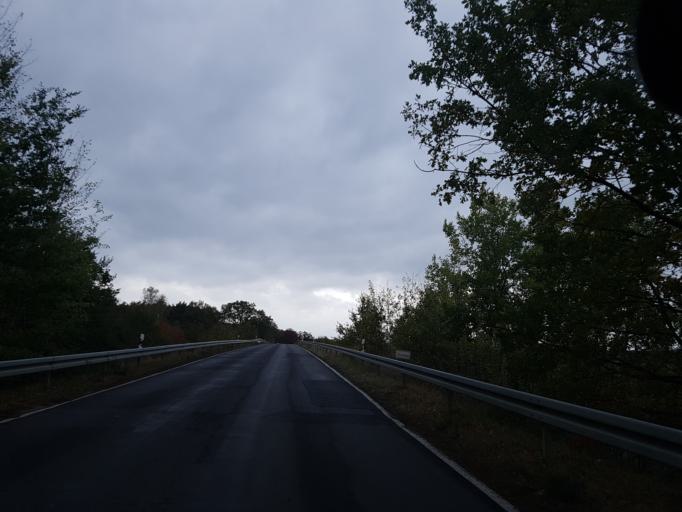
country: DE
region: Brandenburg
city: Herzberg
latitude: 51.6418
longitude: 13.2363
